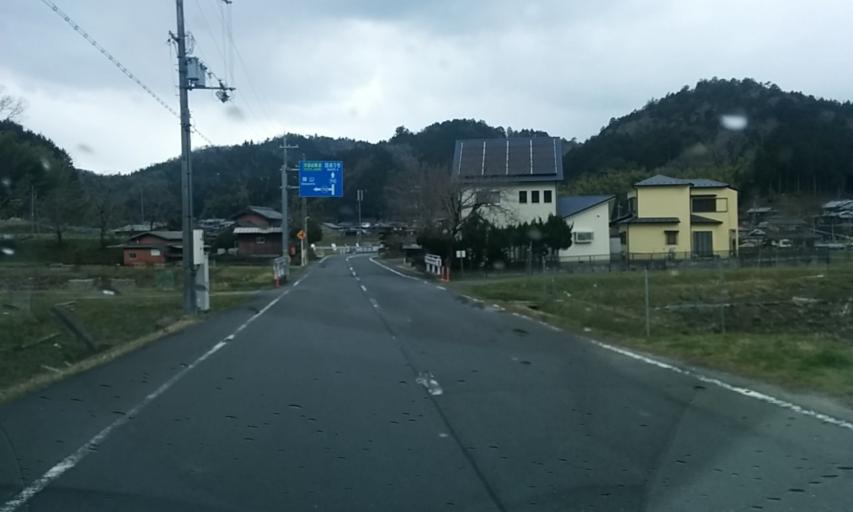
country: JP
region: Hyogo
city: Sasayama
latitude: 35.1254
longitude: 135.4139
